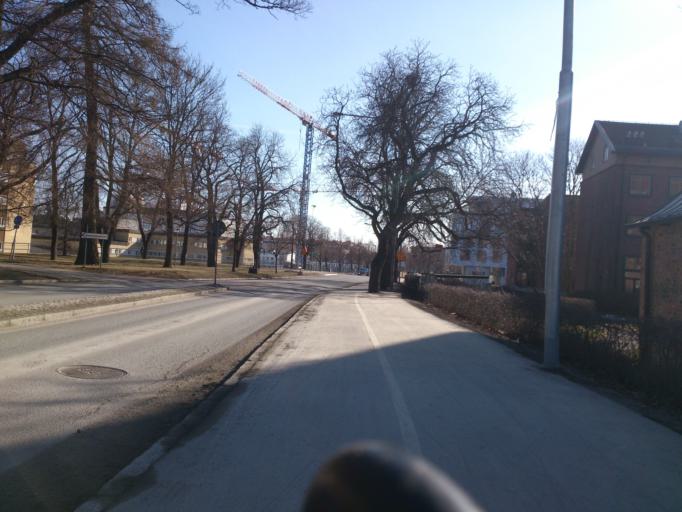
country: SE
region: Uppsala
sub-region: Uppsala Kommun
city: Uppsala
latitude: 59.8500
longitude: 17.6355
